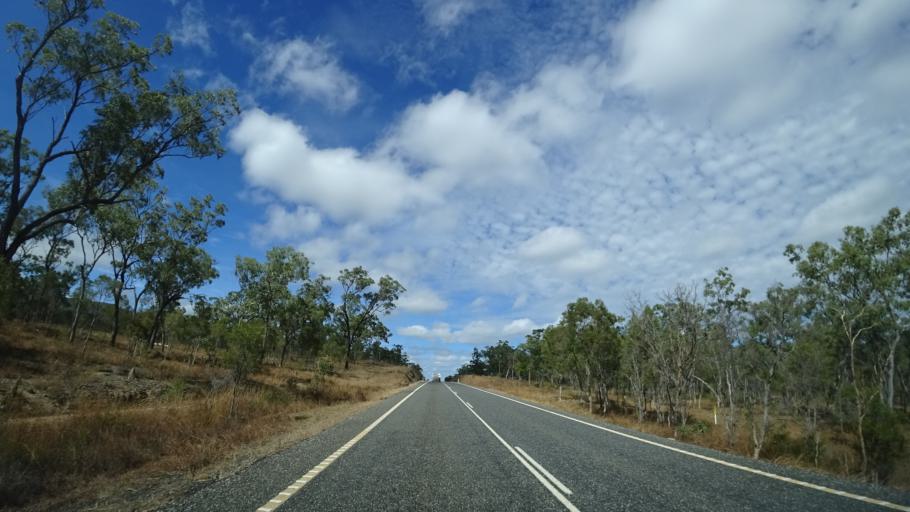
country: AU
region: Queensland
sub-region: Cairns
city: Port Douglas
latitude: -16.3145
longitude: 144.7181
